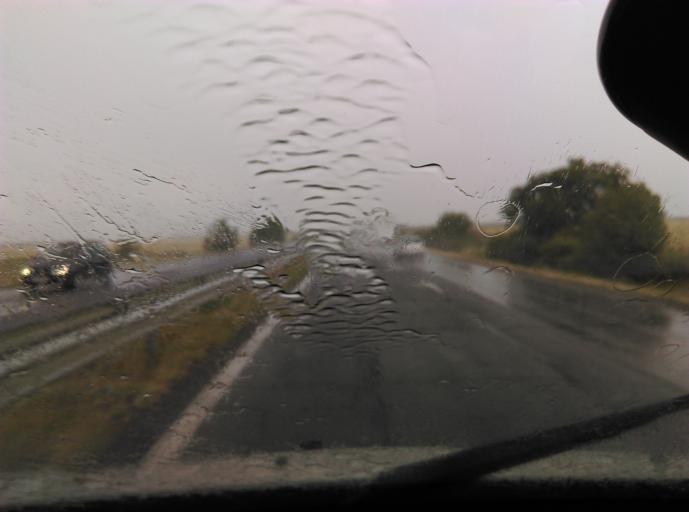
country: BG
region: Burgas
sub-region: Obshtina Burgas
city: Burgas
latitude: 42.5842
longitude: 27.4025
